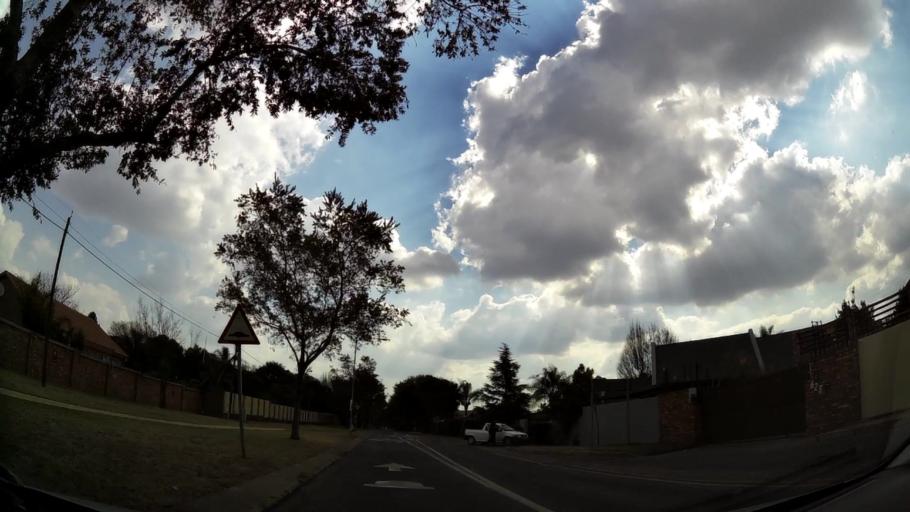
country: ZA
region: Gauteng
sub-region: City of Tshwane Metropolitan Municipality
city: Centurion
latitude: -25.8409
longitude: 28.2624
